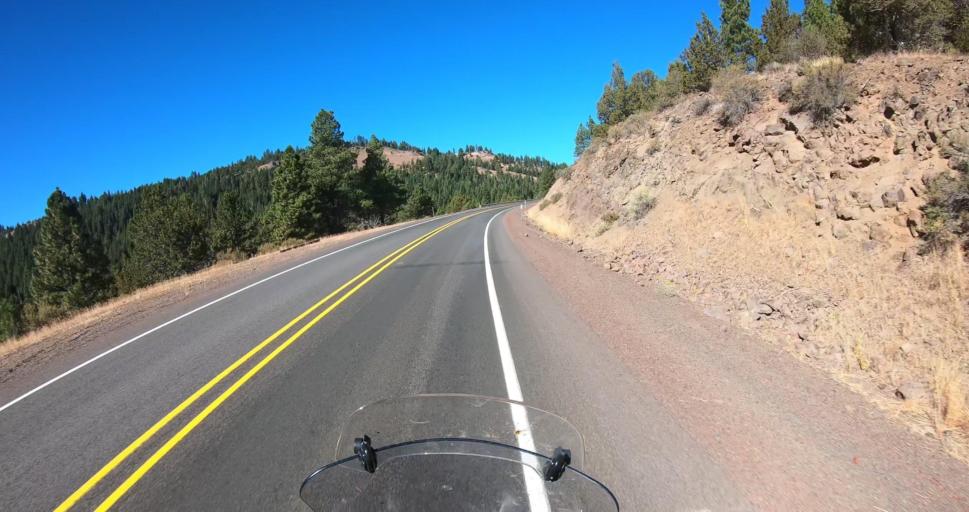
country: US
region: Oregon
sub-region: Lake County
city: Lakeview
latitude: 42.2295
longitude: -120.2852
